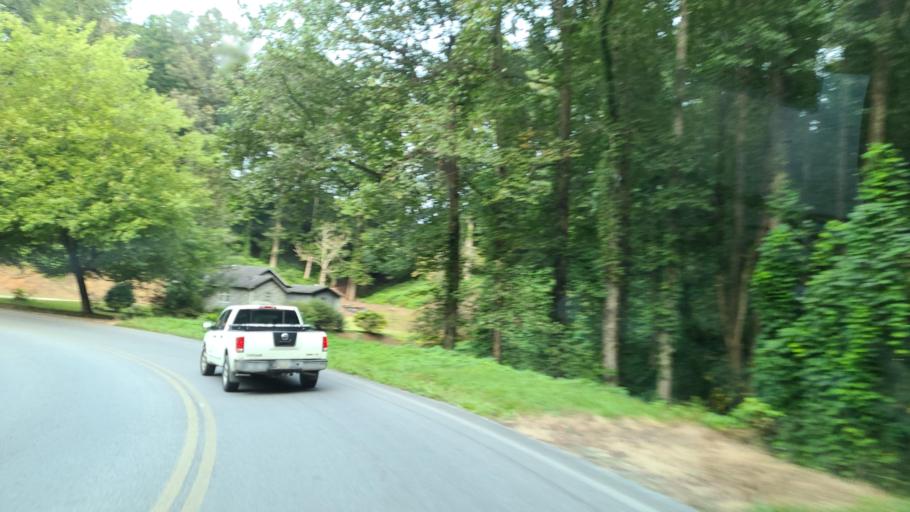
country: US
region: Georgia
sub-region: Fannin County
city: Blue Ridge
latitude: 34.8722
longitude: -84.3307
